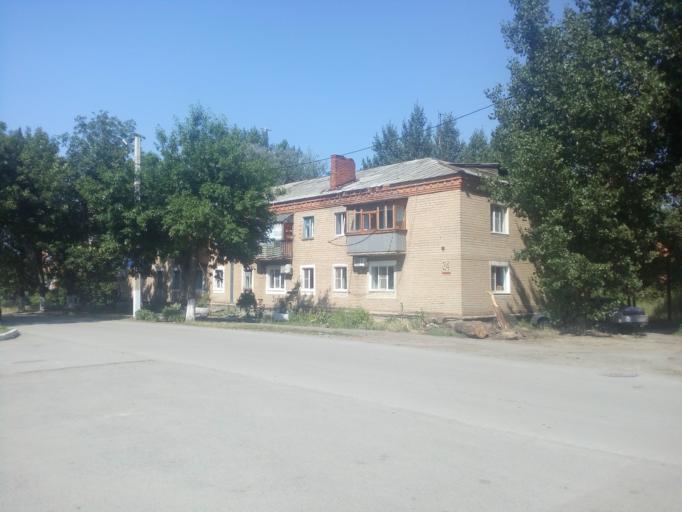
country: RU
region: Rostov
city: Sholokhovskiy
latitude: 48.2832
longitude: 41.0503
